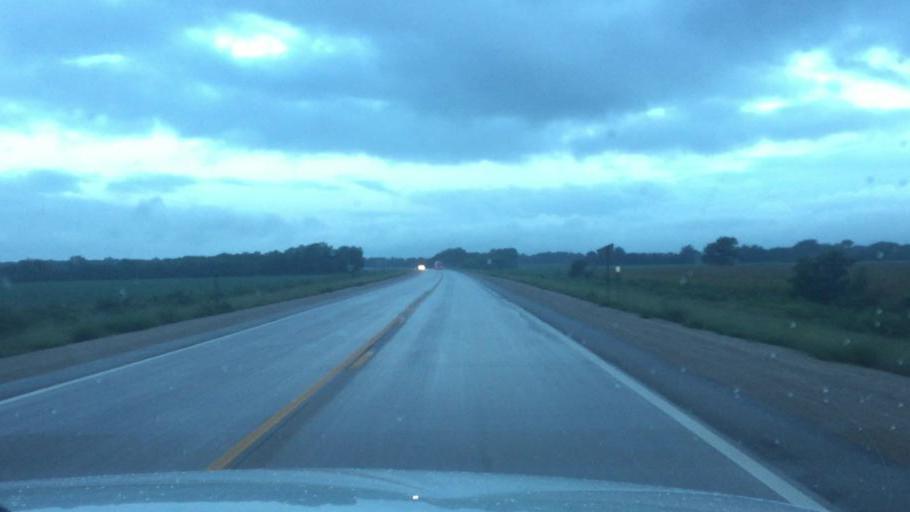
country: US
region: Kansas
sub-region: Neosho County
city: Chanute
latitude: 37.7405
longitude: -95.4432
